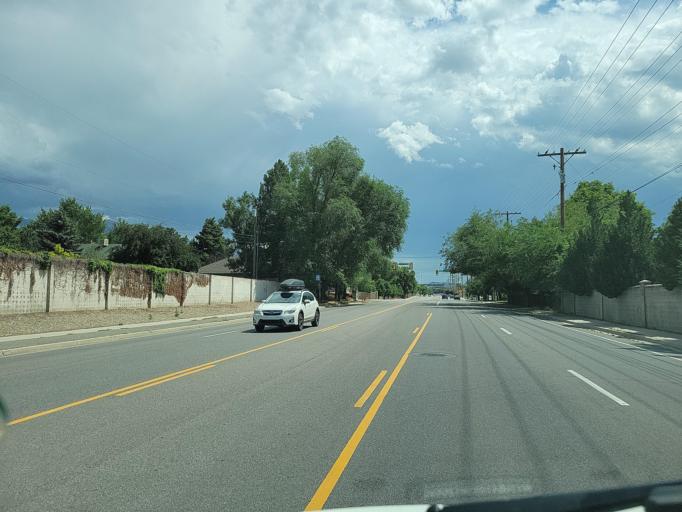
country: US
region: Utah
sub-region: Salt Lake County
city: Little Cottonwood Creek Valley
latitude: 40.6357
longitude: -111.8547
